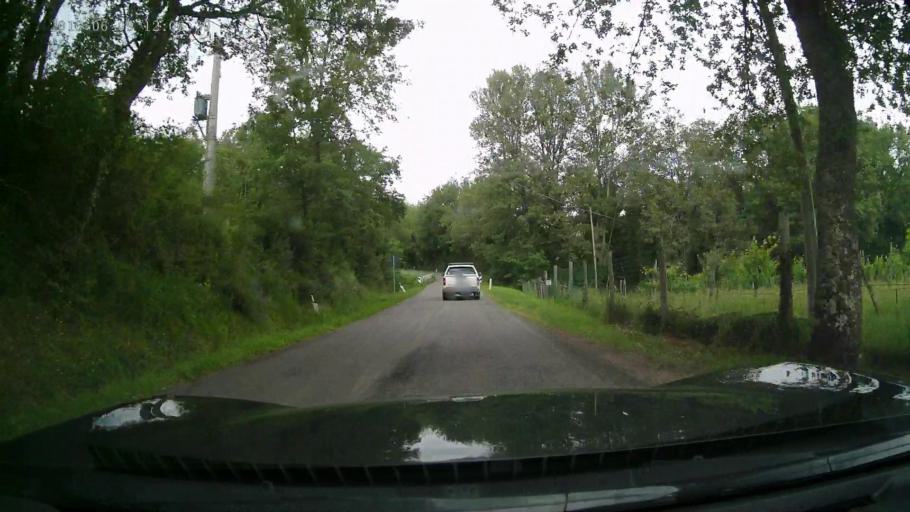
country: IT
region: Tuscany
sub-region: Province of Florence
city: Panzano in Chianti
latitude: 43.5260
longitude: 11.2903
